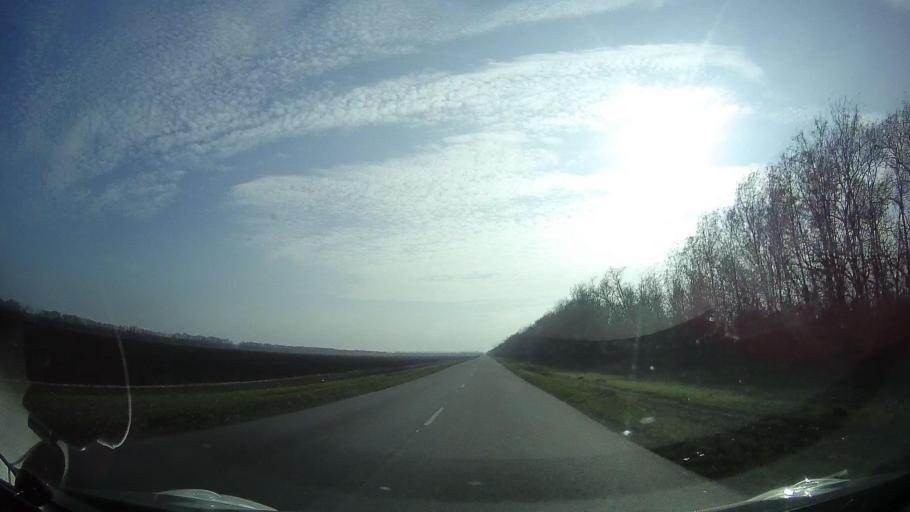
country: RU
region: Rostov
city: Mechetinskaya
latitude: 46.8858
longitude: 40.5419
